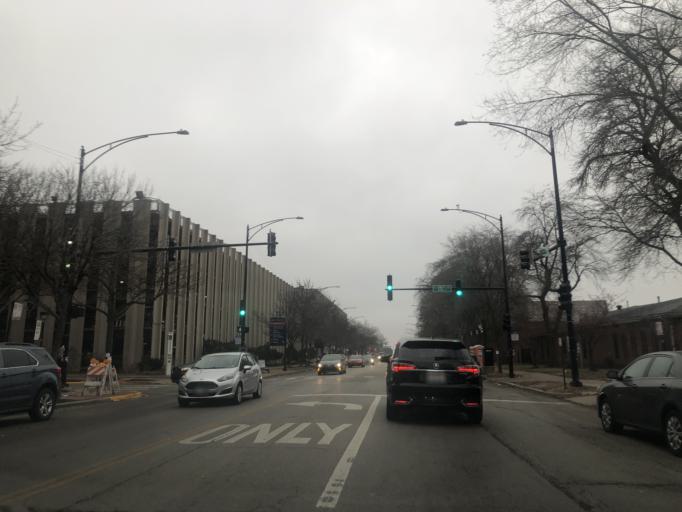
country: US
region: Illinois
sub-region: Cook County
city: Chicago
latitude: 41.7899
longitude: -87.6061
